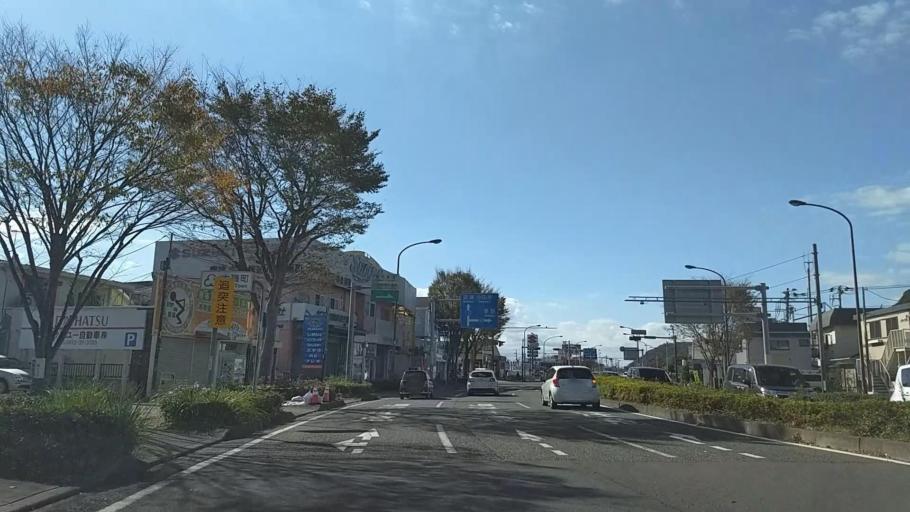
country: JP
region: Kanagawa
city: Hiratsuka
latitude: 35.3251
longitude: 139.3316
